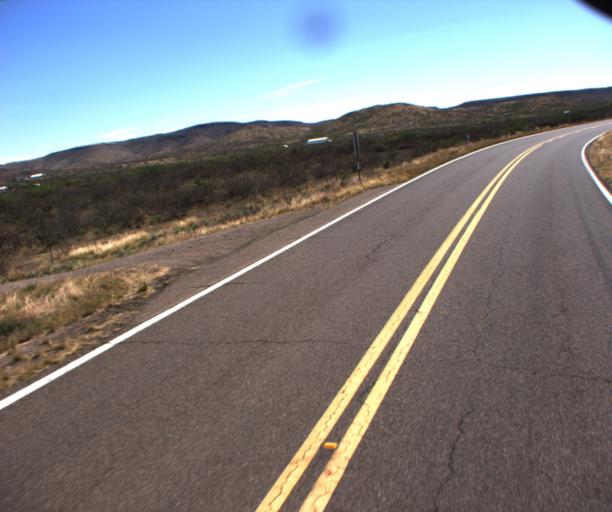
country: US
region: Arizona
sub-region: Cochise County
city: Douglas
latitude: 31.4905
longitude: -109.4242
